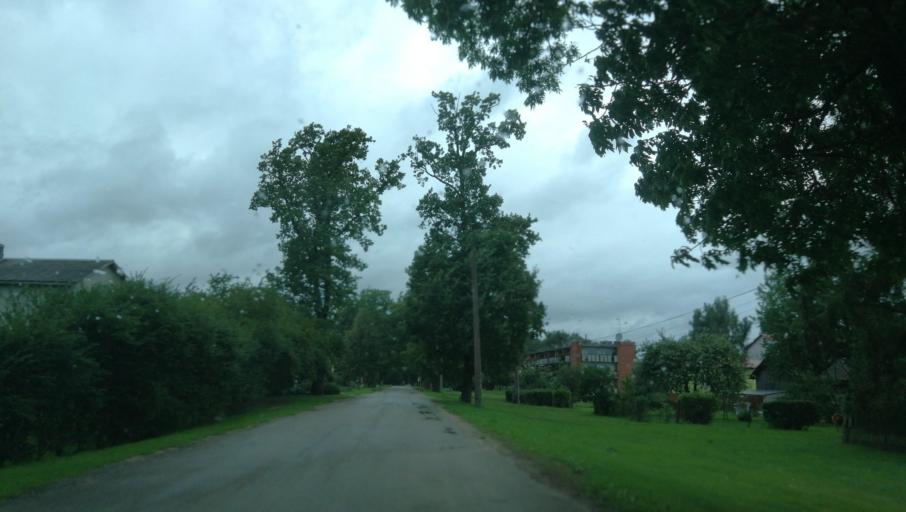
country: LV
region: Beverina
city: Murmuiza
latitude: 57.4719
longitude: 25.4933
